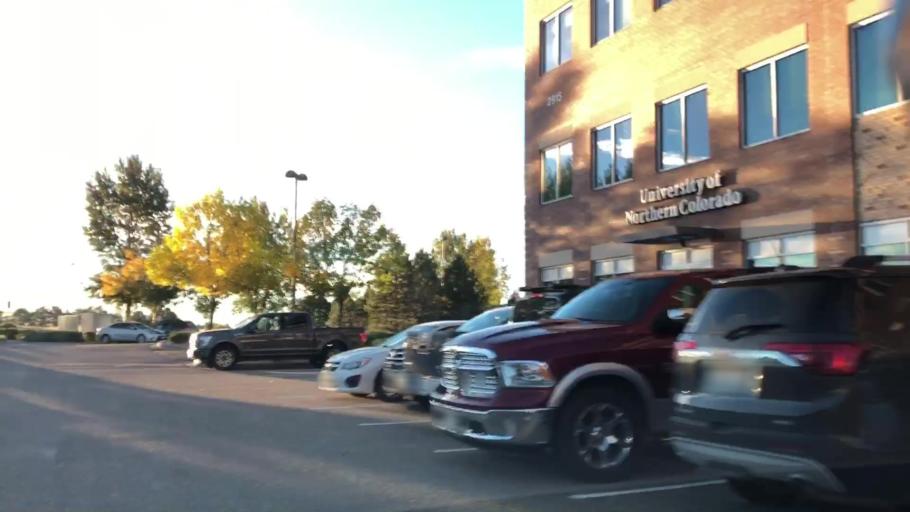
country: US
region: Colorado
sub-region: Larimer County
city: Loveland
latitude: 40.4215
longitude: -105.0027
